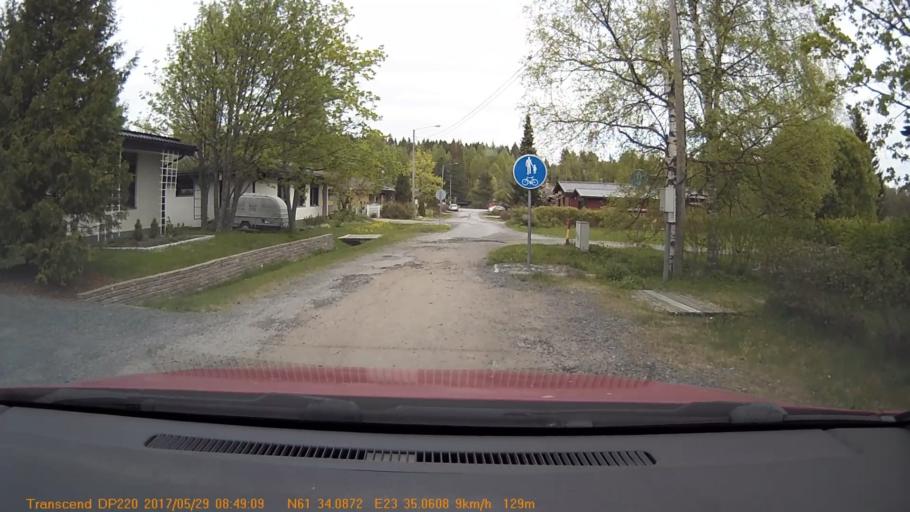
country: FI
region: Pirkanmaa
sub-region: Tampere
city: Yloejaervi
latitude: 61.5680
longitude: 23.5839
